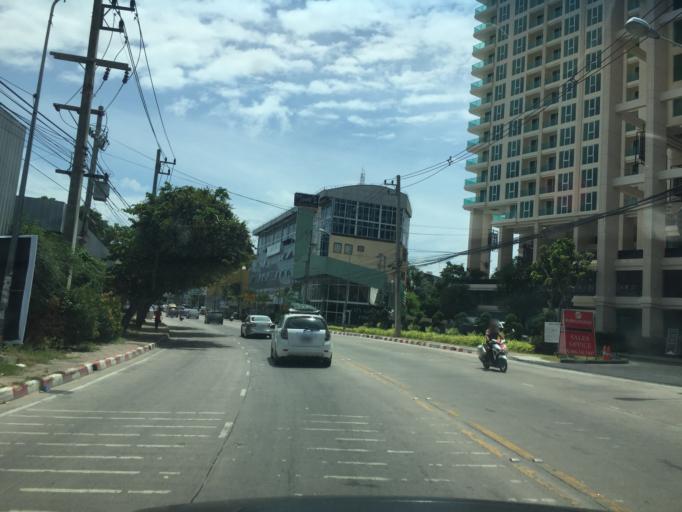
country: TH
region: Chon Buri
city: Phatthaya
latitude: 12.9210
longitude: 100.8815
